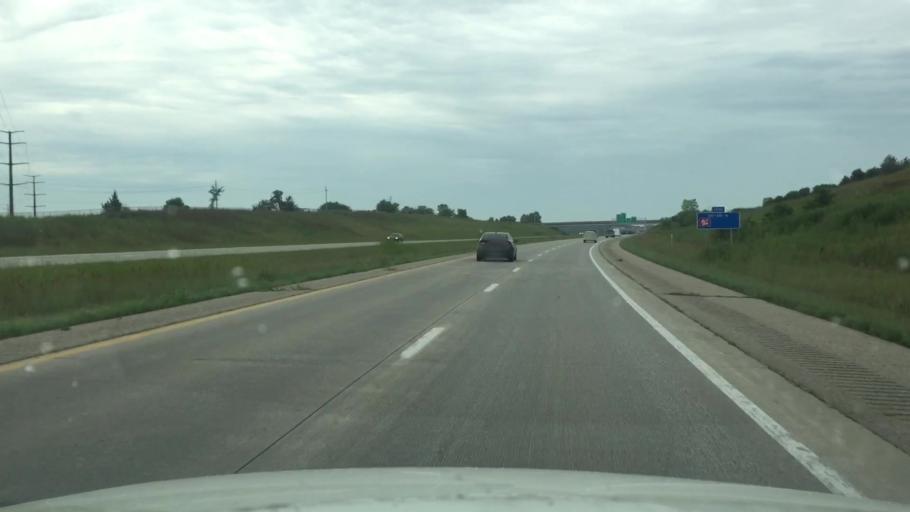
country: US
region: Iowa
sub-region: Warren County
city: Norwalk
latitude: 41.4981
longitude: -93.6096
